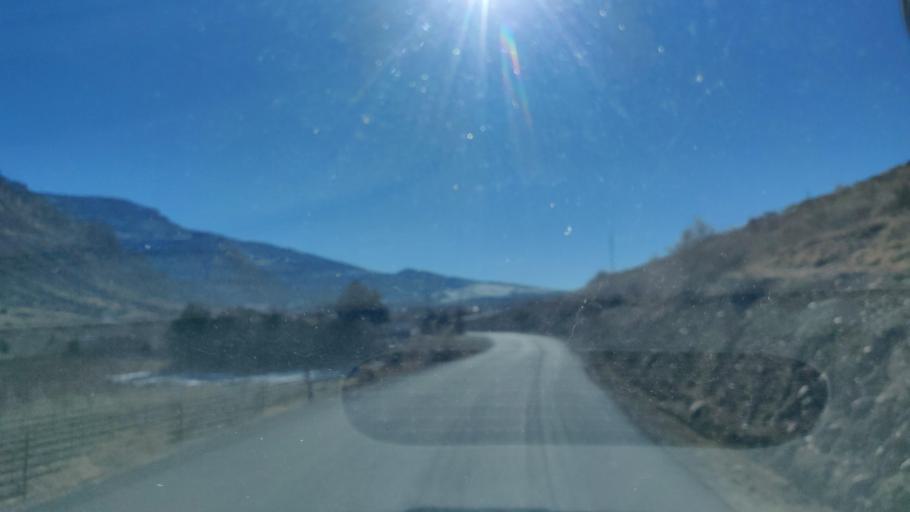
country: US
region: Colorado
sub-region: Mesa County
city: Palisade
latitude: 39.1007
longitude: -108.3309
